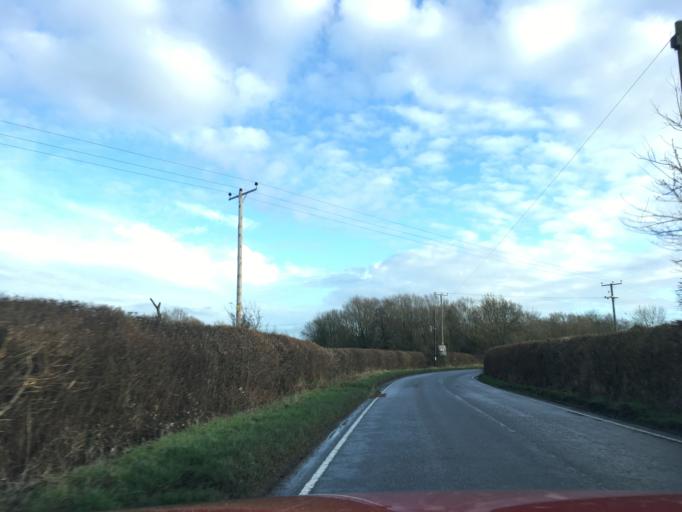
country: GB
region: England
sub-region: Warwickshire
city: Alcester
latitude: 52.2274
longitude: -1.8254
